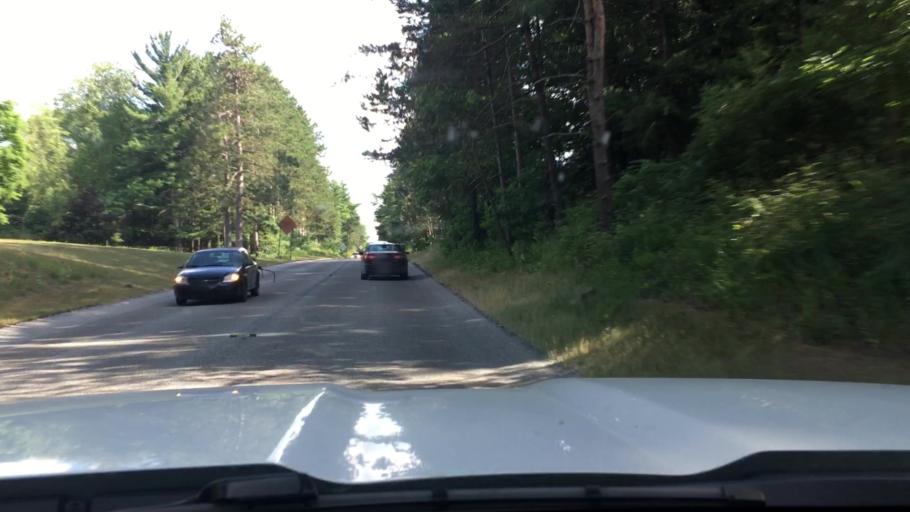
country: US
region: Michigan
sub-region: Montcalm County
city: Greenville
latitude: 43.1695
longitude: -85.3528
